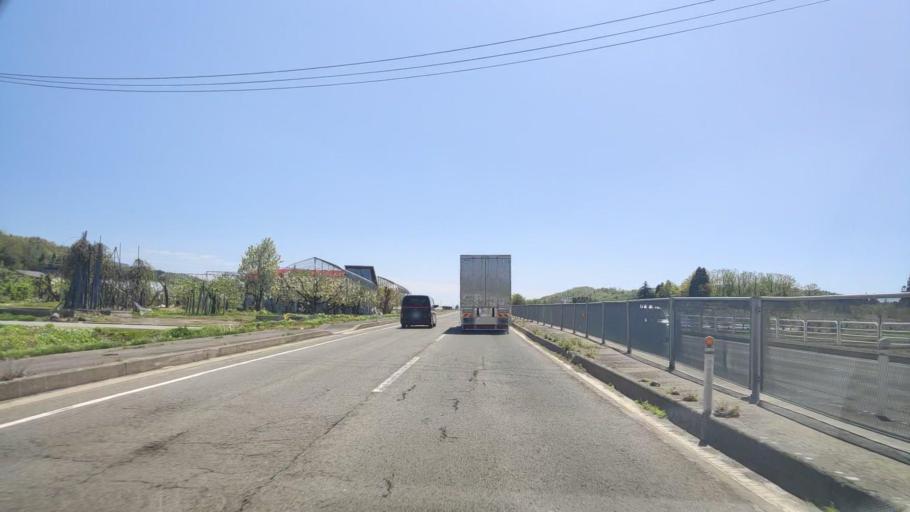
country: JP
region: Yamagata
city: Obanazawa
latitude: 38.5373
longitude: 140.3941
